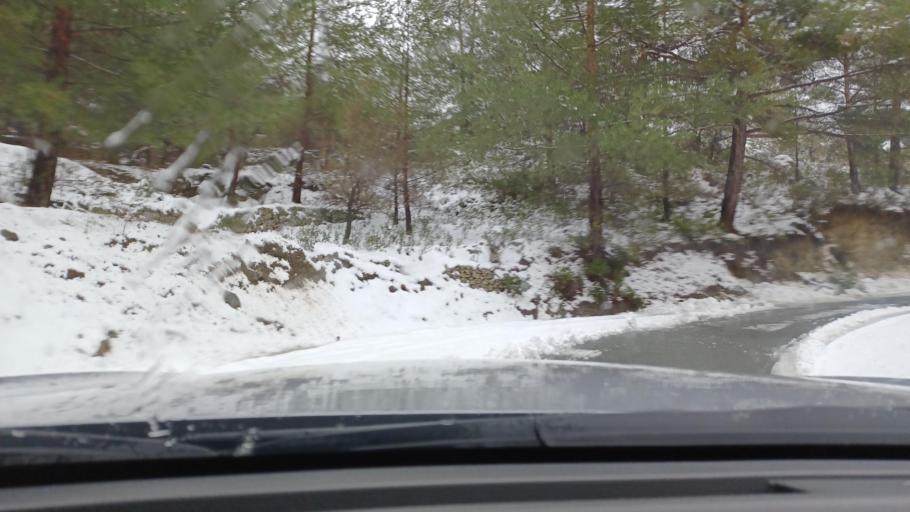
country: CY
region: Limassol
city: Pelendri
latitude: 34.9124
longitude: 32.9536
